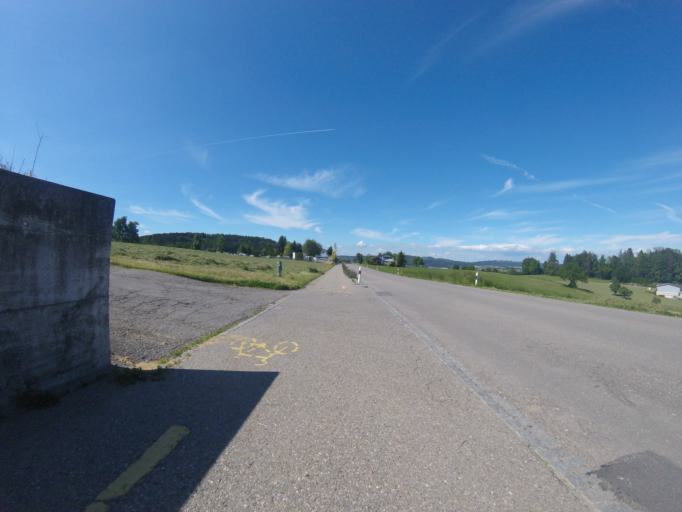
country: CH
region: Saint Gallen
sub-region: Wahlkreis Toggenburg
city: Kirchberg
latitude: 47.4221
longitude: 9.0623
